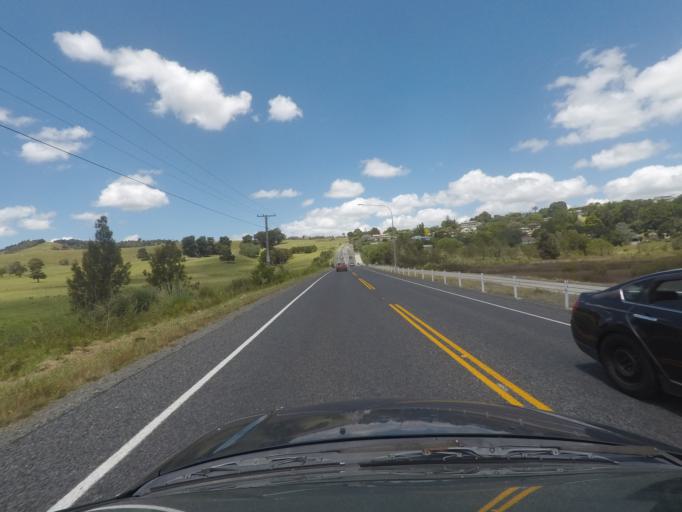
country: NZ
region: Northland
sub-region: Whangarei
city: Whangarei
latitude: -35.7397
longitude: 174.3618
